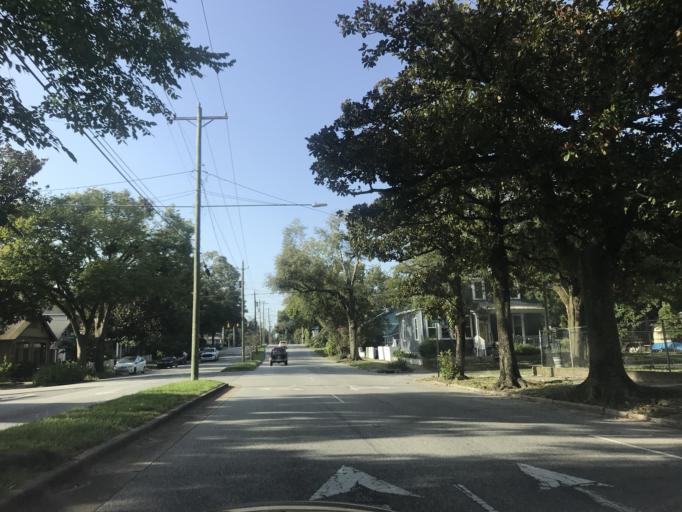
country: US
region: North Carolina
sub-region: New Hanover County
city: Wilmington
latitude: 34.2264
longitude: -77.9449
